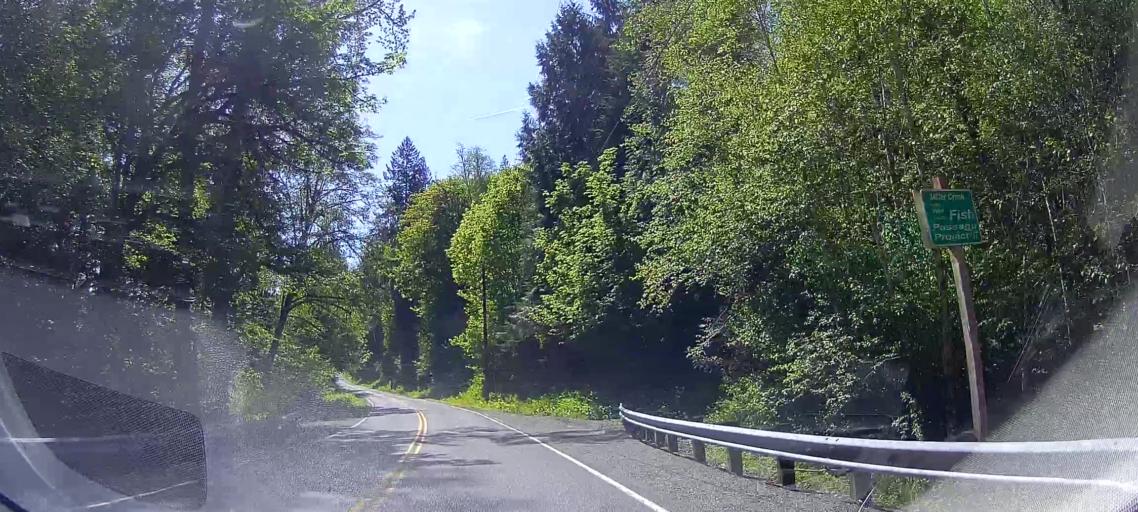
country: US
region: Washington
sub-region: Snohomish County
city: Darrington
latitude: 48.4837
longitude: -121.6544
